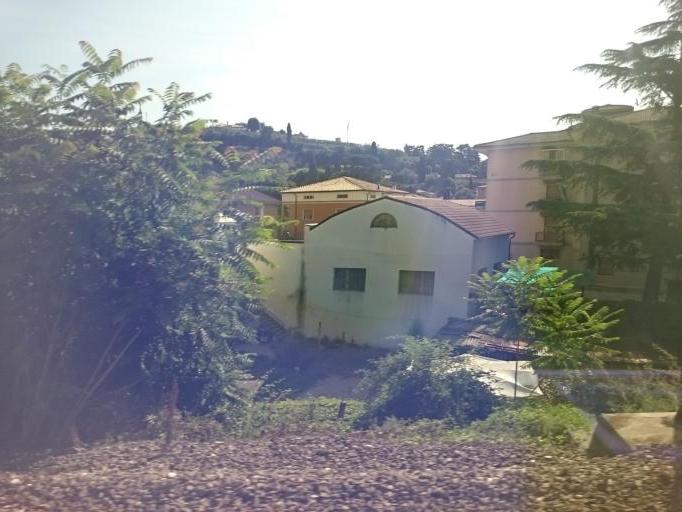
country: IT
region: Veneto
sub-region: Provincia di Verona
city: Sant'Ambrogio di Valpollicella
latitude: 45.5186
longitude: 10.8207
